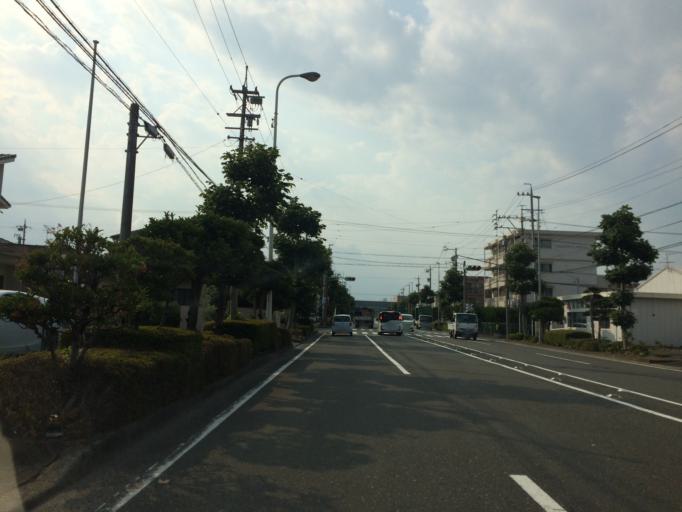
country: JP
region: Shizuoka
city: Shizuoka-shi
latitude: 34.9559
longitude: 138.4190
